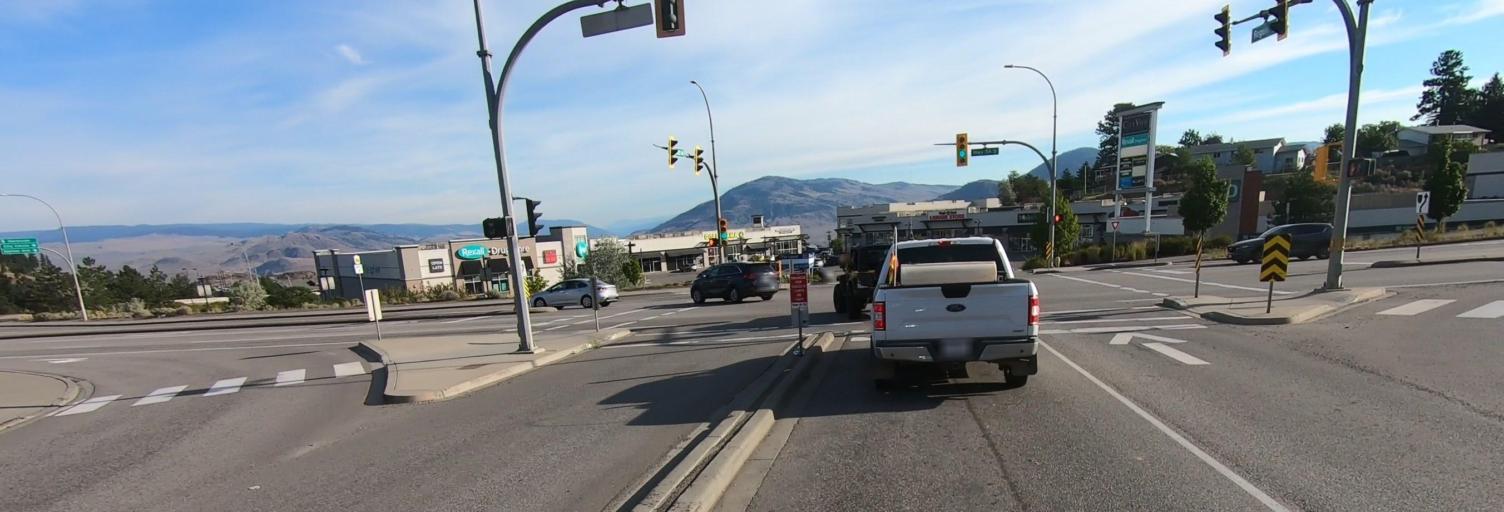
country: CA
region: British Columbia
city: Kamloops
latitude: 50.6521
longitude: -120.3674
